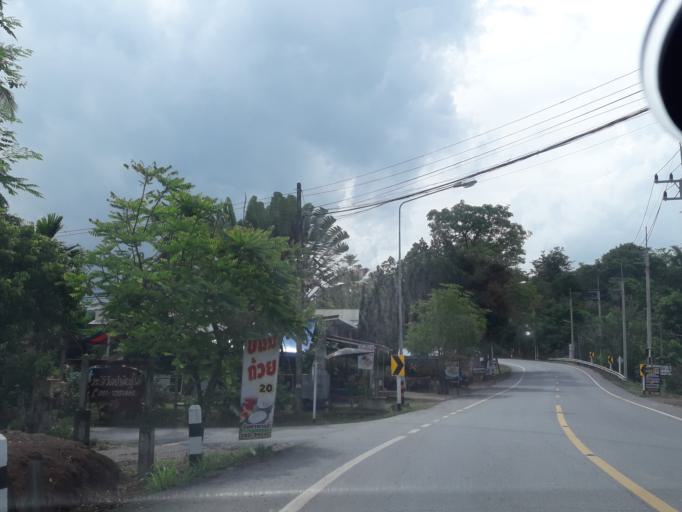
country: TH
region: Sara Buri
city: Wihan Daeng
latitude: 14.4079
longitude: 101.1023
